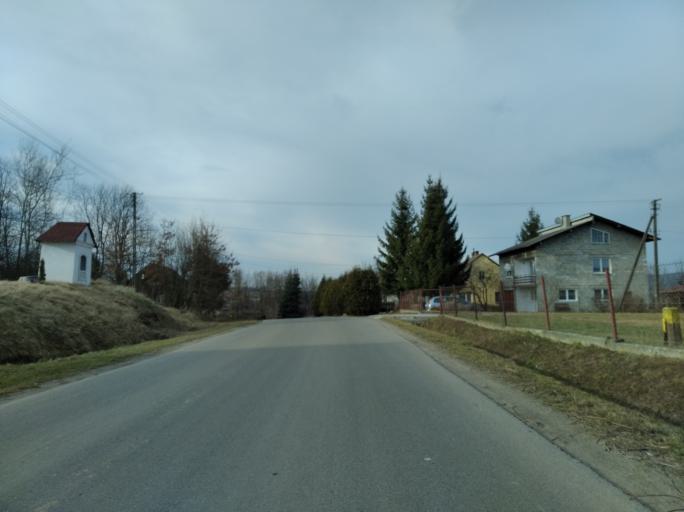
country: PL
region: Subcarpathian Voivodeship
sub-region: Powiat brzozowski
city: Blizne
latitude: 49.7332
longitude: 21.9844
